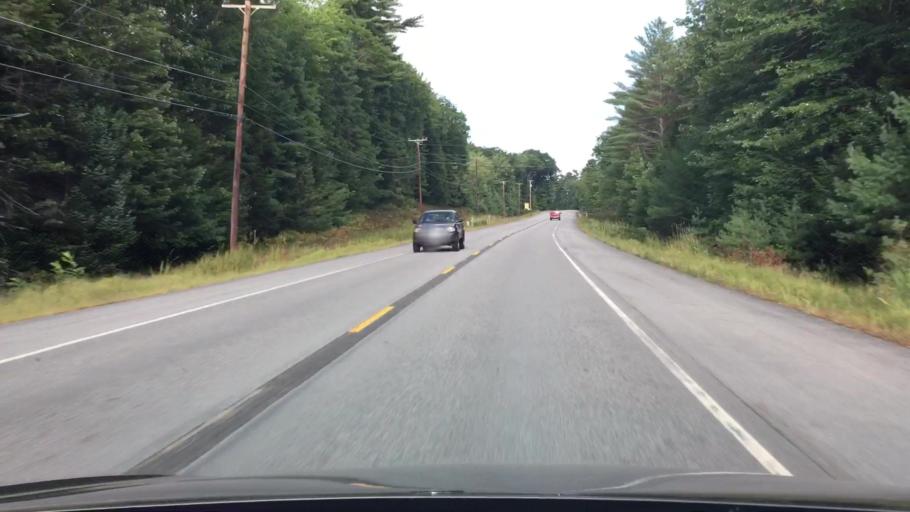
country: US
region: Maine
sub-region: Cumberland County
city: Bridgton
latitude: 44.0677
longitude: -70.7905
